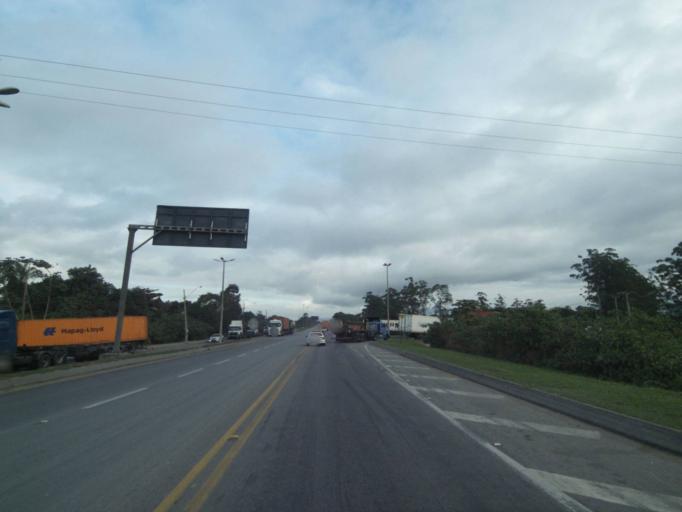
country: BR
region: Parana
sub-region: Paranagua
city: Paranagua
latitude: -25.5437
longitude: -48.5595
